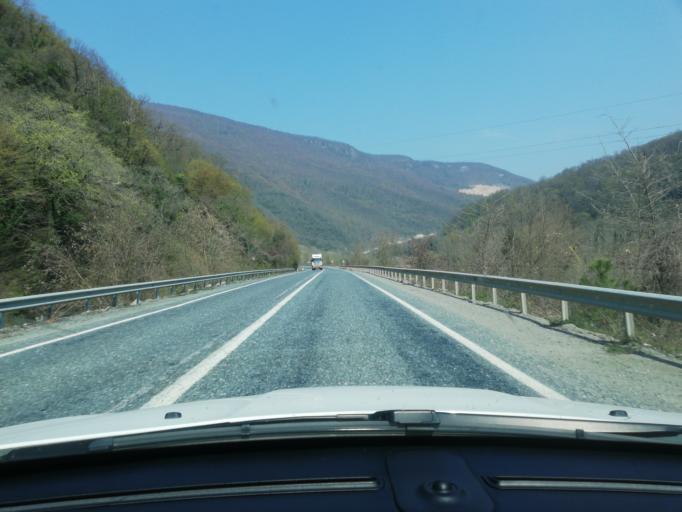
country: TR
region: Zonguldak
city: Gokcebey
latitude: 41.2600
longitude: 32.1553
